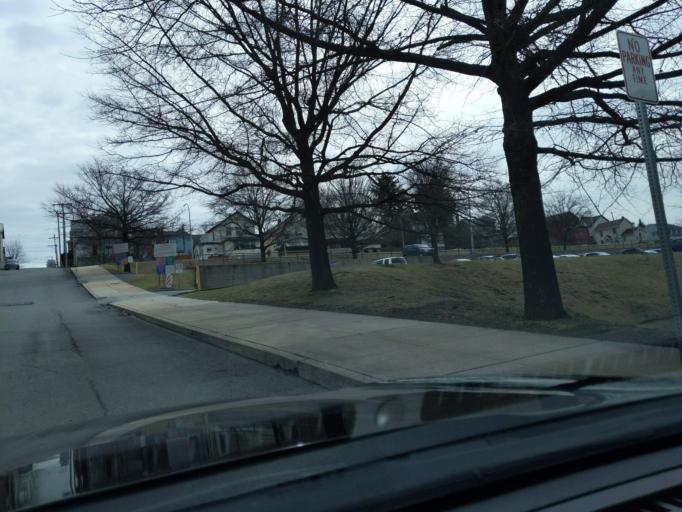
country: US
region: Pennsylvania
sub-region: Blair County
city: Altoona
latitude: 40.5110
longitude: -78.3960
